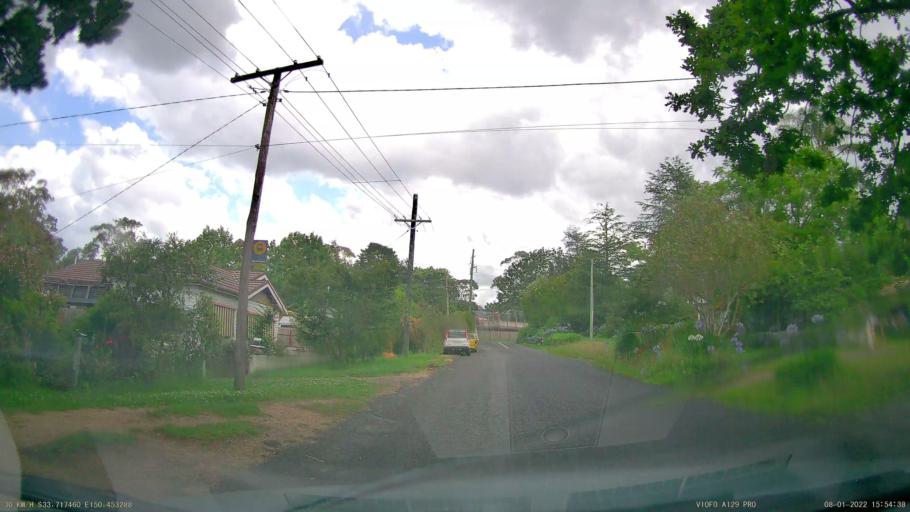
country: AU
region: New South Wales
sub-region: Blue Mountains Municipality
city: Hazelbrook
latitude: -33.7176
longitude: 150.4532
